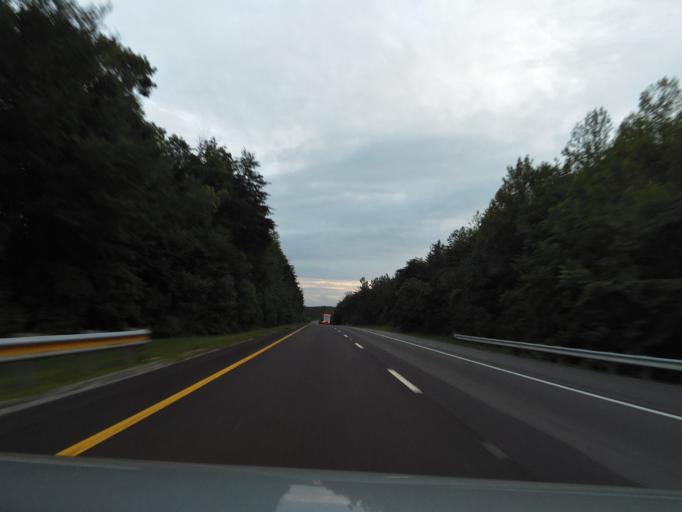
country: US
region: Tennessee
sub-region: Campbell County
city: Jacksboro
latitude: 36.4577
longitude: -84.2580
